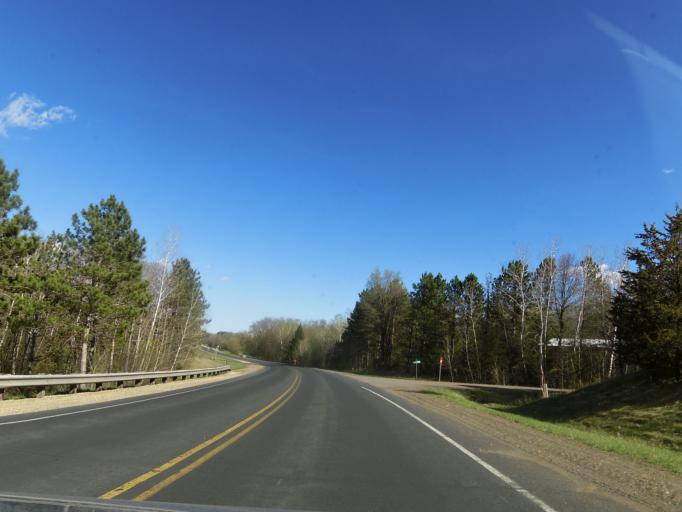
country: US
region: Minnesota
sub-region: Washington County
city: Bayport
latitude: 45.0504
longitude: -92.7207
